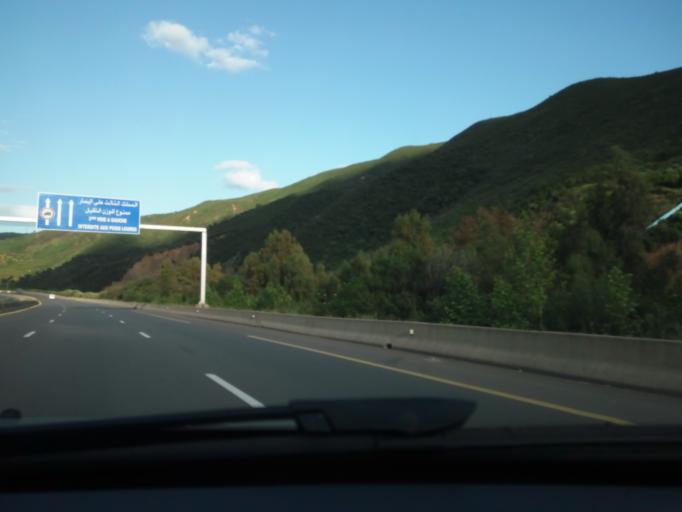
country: DZ
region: Tipaza
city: El Affroun
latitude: 36.3910
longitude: 2.5168
